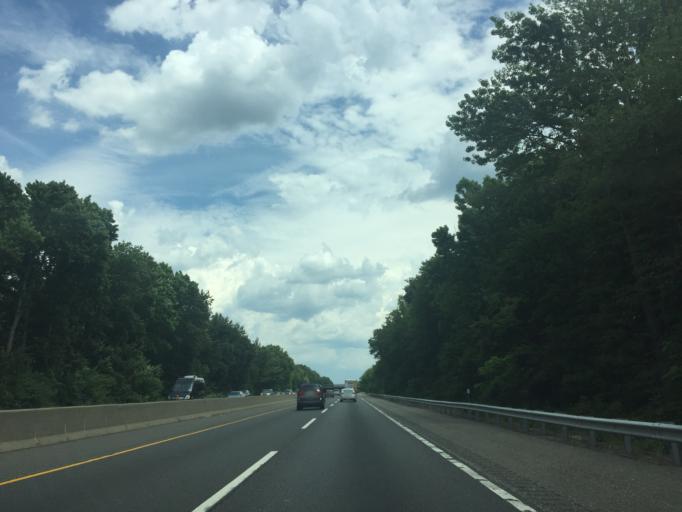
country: US
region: New Jersey
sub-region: Camden County
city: Barrington
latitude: 39.8617
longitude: -75.0630
